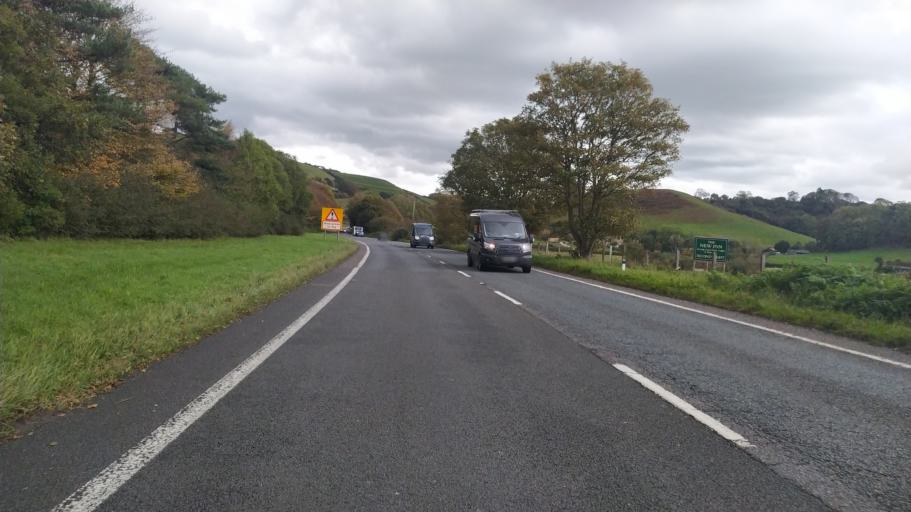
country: GB
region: England
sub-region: Dorset
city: Bridport
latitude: 50.7354
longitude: -2.7334
